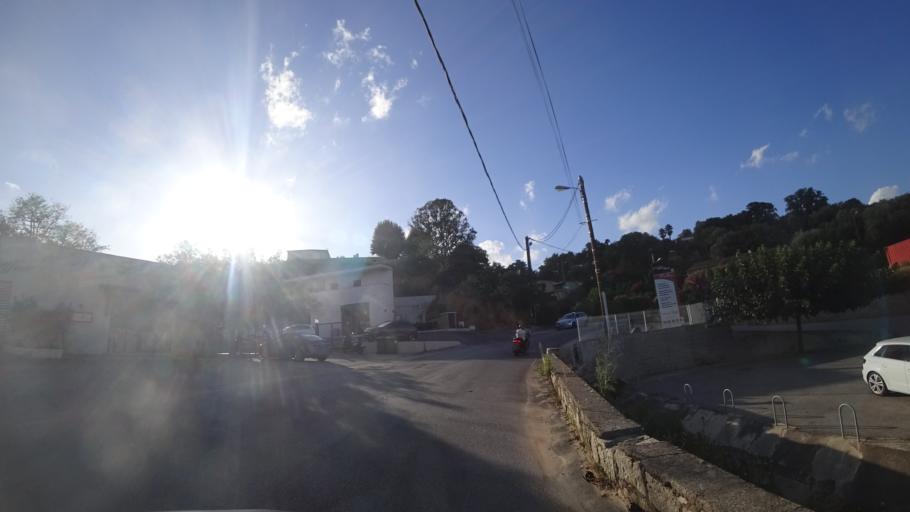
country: FR
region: Corsica
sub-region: Departement de la Corse-du-Sud
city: Ajaccio
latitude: 41.9425
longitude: 8.7346
